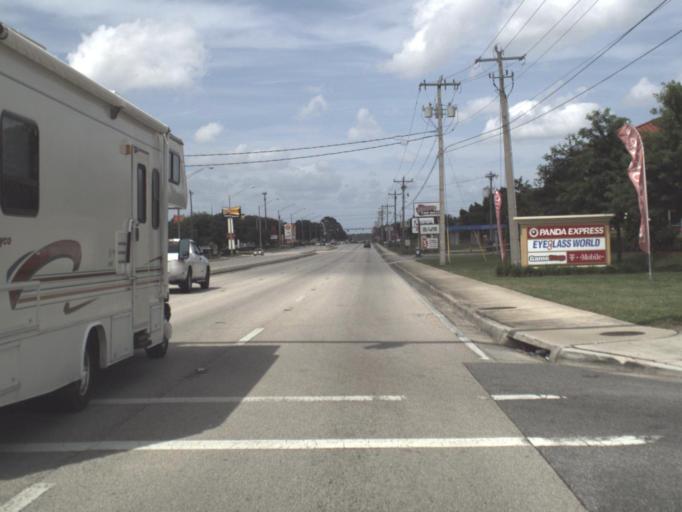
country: US
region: Florida
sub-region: Clay County
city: Lakeside
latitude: 30.1396
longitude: -81.7711
